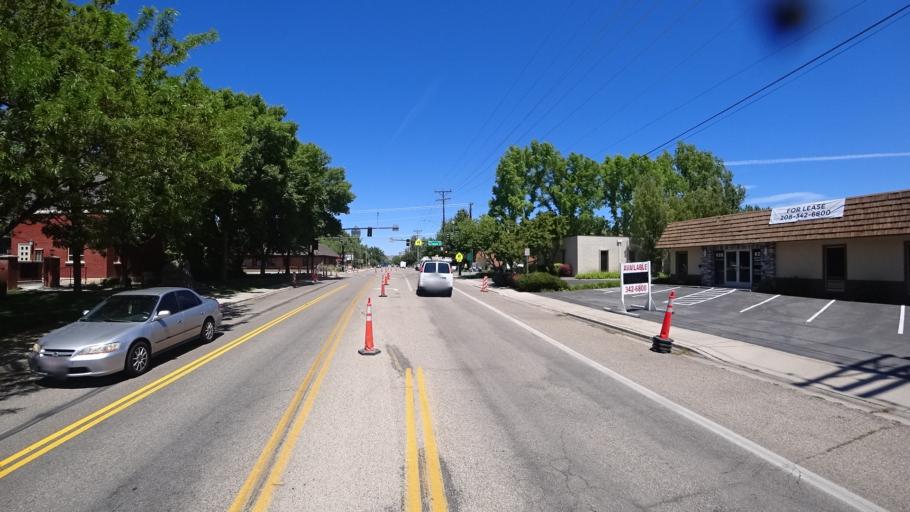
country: US
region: Idaho
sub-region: Ada County
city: Garden City
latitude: 43.5966
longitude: -116.2286
